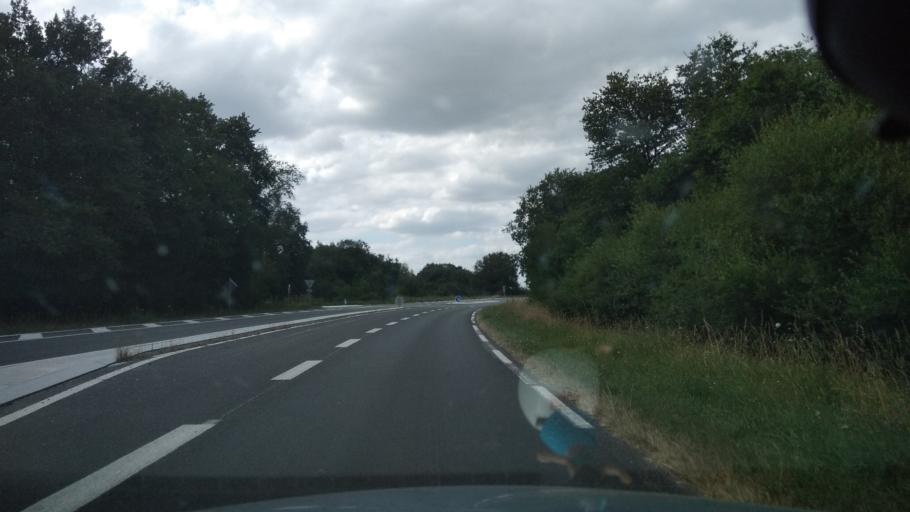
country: FR
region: Poitou-Charentes
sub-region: Departement de la Vienne
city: Les Ormes
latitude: 46.9964
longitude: 0.5952
